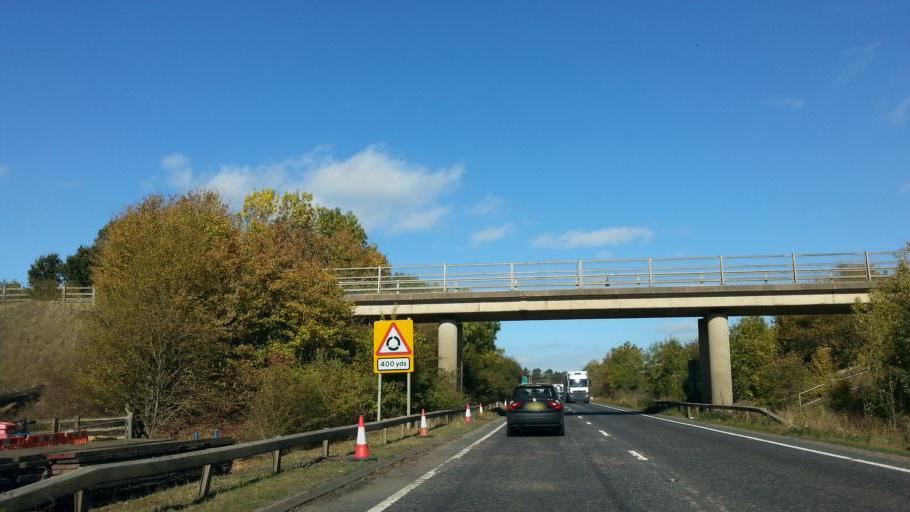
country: GB
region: England
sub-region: Northamptonshire
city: Thrapston
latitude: 52.3873
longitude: -0.5235
